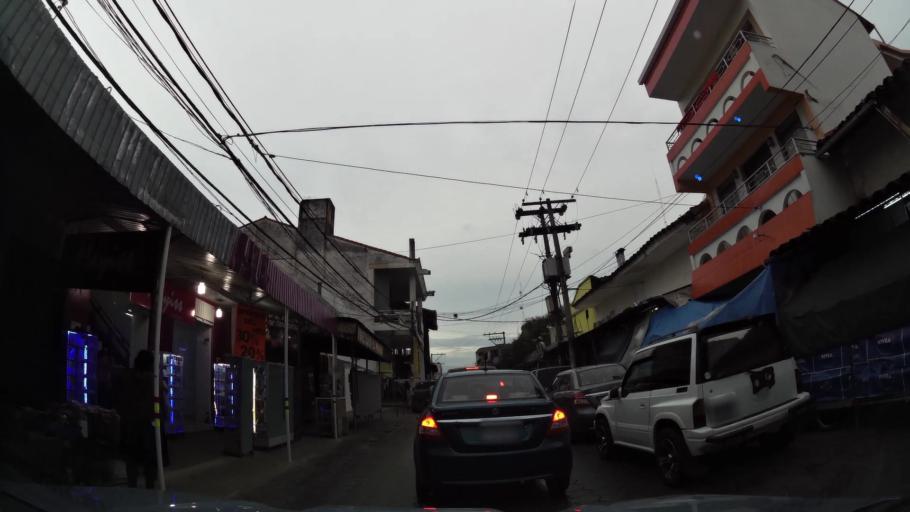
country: BO
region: Santa Cruz
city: Santa Cruz de la Sierra
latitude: -17.7861
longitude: -63.1853
